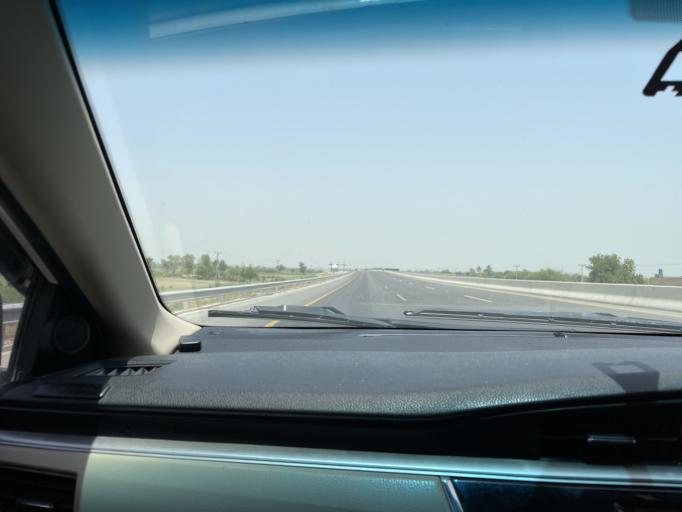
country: PK
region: Sindh
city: Ghotki
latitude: 28.0184
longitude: 69.2890
